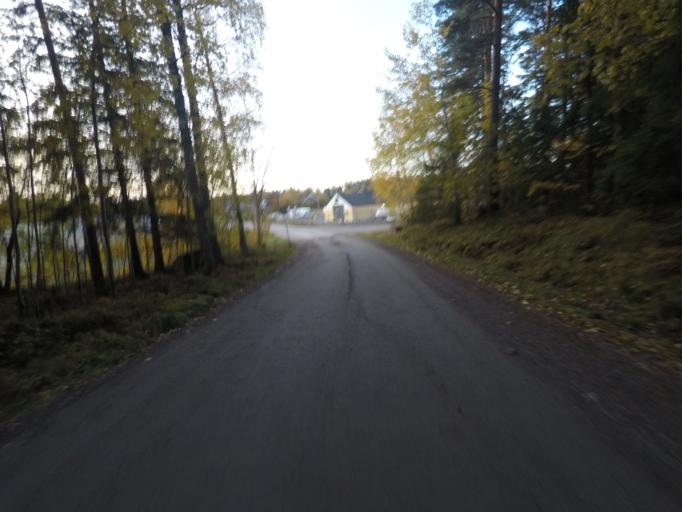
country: SE
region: OErebro
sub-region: Karlskoga Kommun
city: Karlskoga
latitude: 59.3023
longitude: 14.5006
